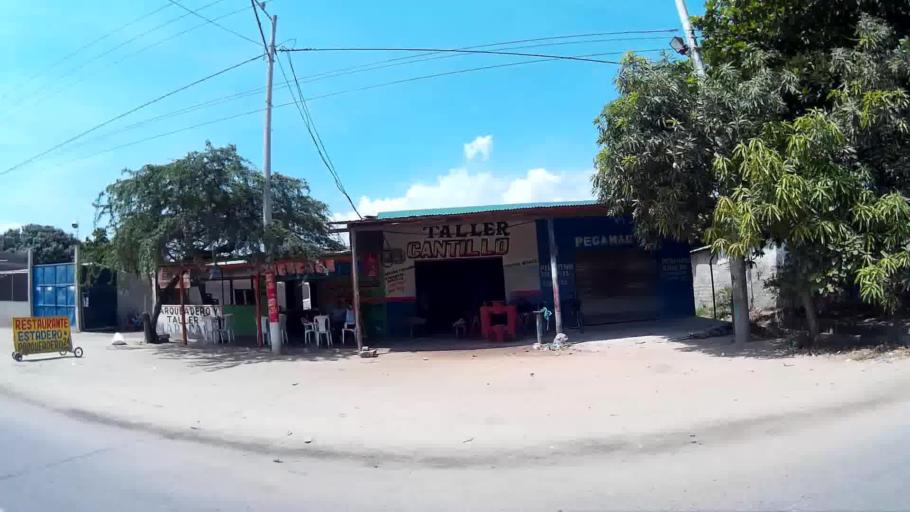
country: CO
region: Magdalena
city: Cienaga
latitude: 11.0055
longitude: -74.2410
